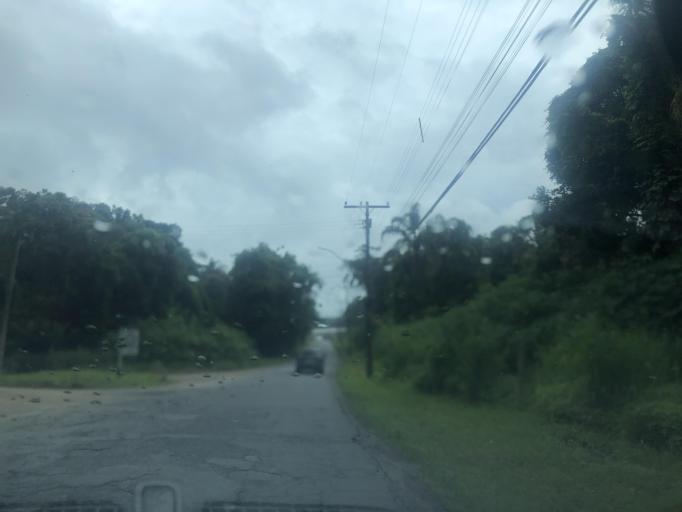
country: BR
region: Santa Catarina
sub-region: Sao Francisco Do Sul
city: Sao Francisco do Sul
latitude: -26.2343
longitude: -48.6130
